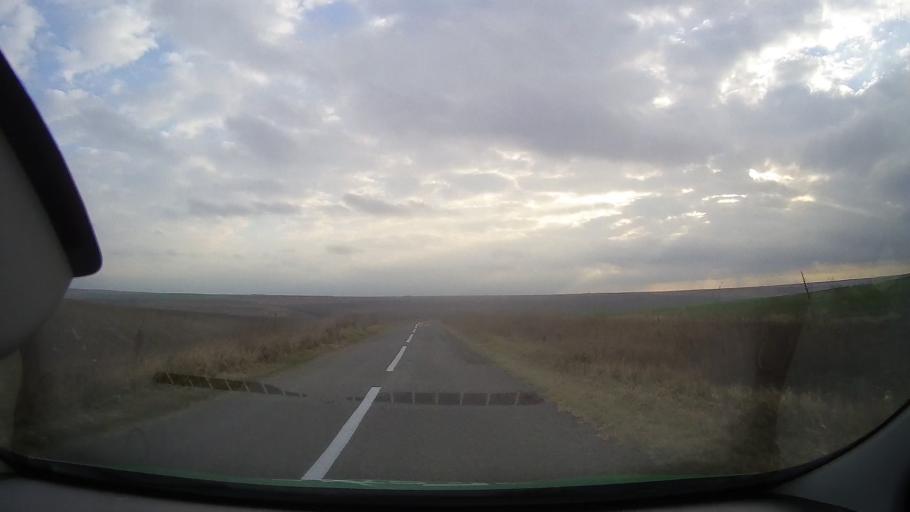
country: RO
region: Constanta
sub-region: Comuna Deleni
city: Pietreni
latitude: 44.1217
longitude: 28.1044
